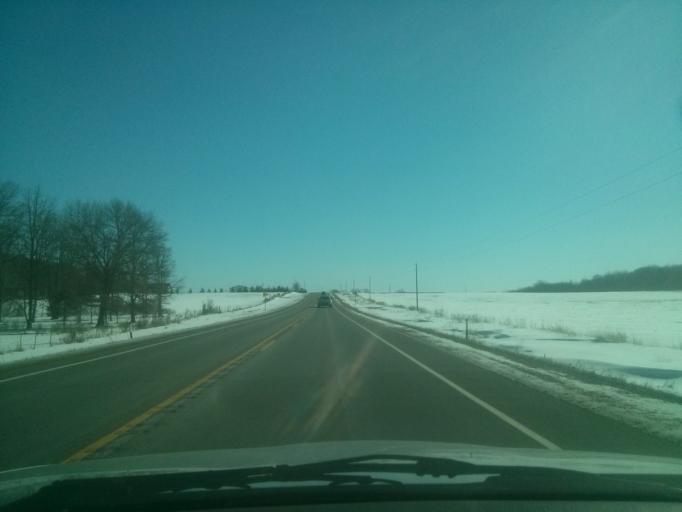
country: US
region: Wisconsin
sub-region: Polk County
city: Clear Lake
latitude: 45.1363
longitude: -92.3119
